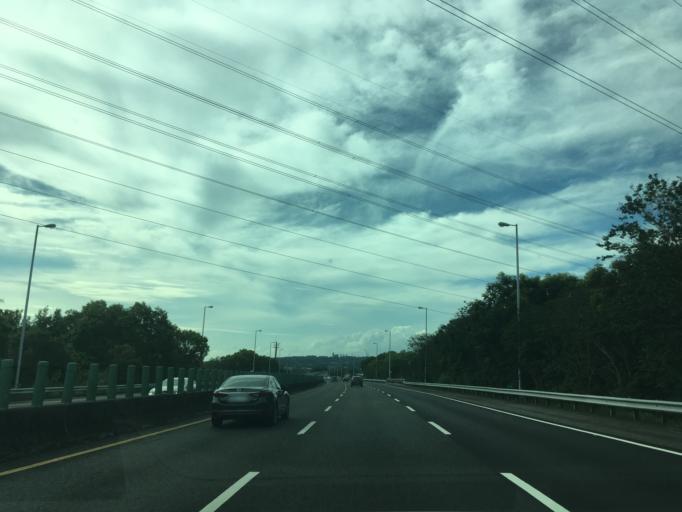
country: TW
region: Taiwan
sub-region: Chiayi
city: Jiayi Shi
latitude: 23.5018
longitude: 120.4922
